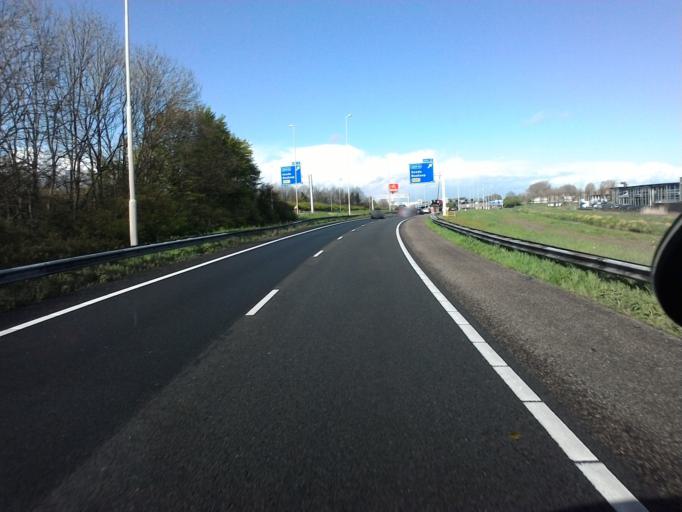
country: NL
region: South Holland
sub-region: Gemeente Waddinxveen
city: Waddinxveen
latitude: 52.0219
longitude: 4.6558
